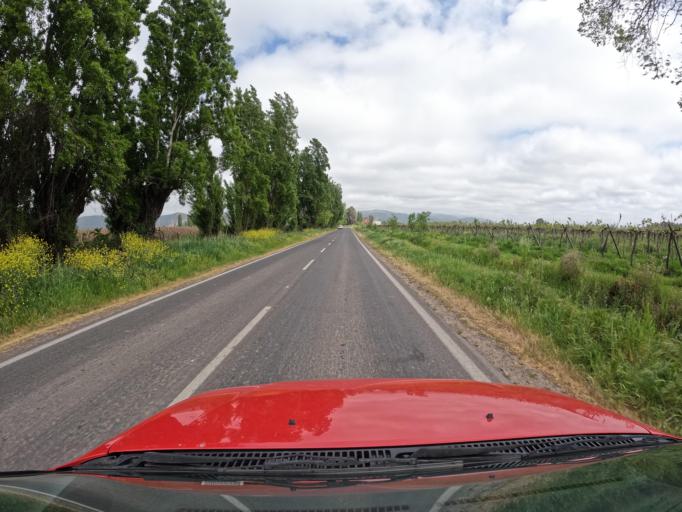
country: CL
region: O'Higgins
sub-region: Provincia de Colchagua
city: Santa Cruz
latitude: -34.6762
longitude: -71.3680
